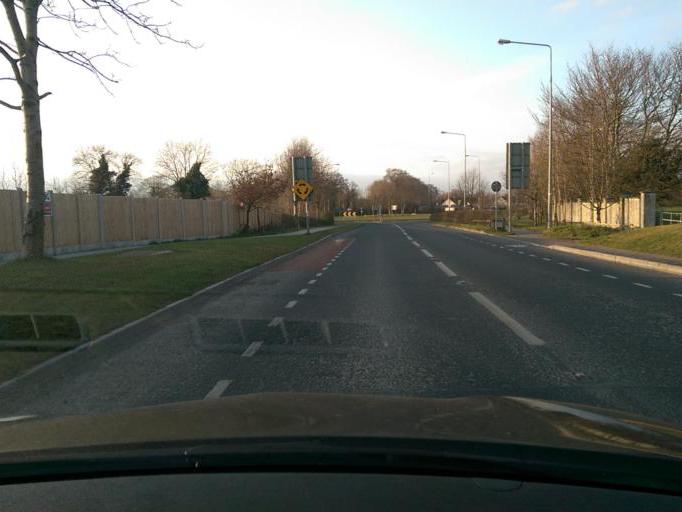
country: IE
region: Munster
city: Nenagh Bridge
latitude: 52.8760
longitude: -8.2018
